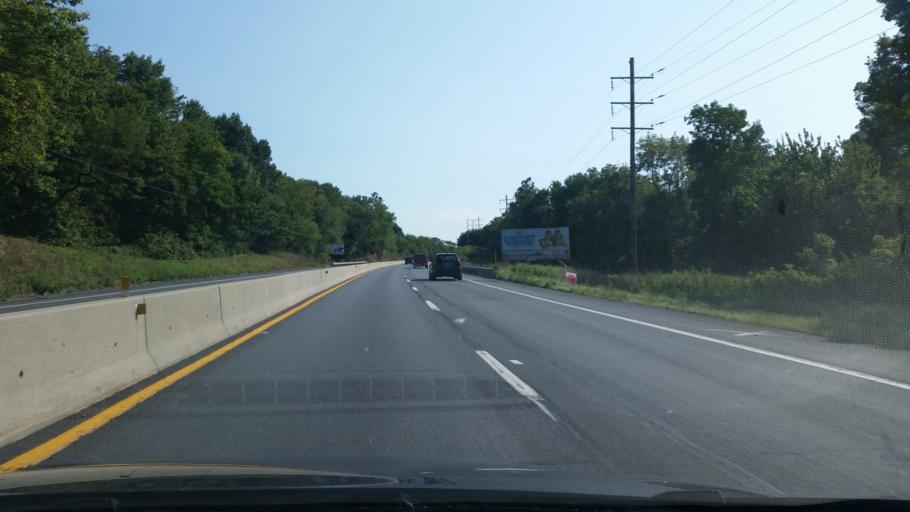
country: US
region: Pennsylvania
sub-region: Berks County
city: Shoemakersville
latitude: 40.4812
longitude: -75.9646
